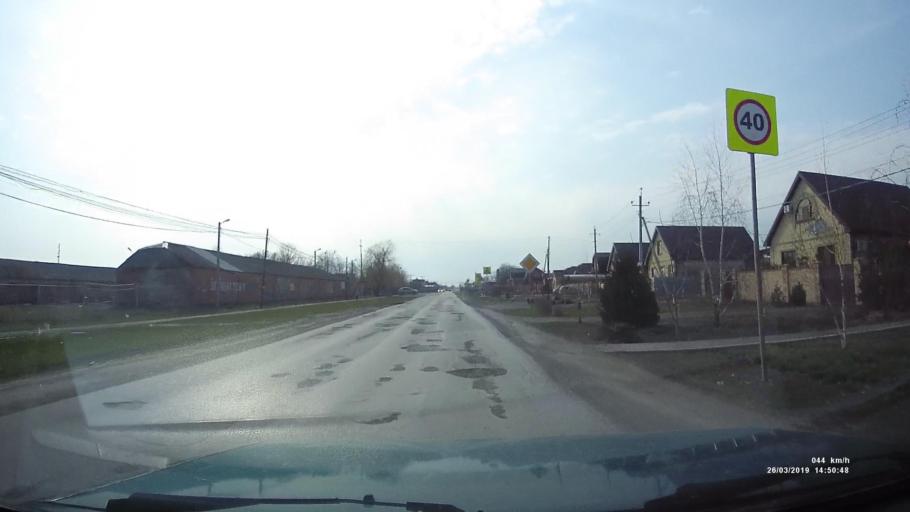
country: RU
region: Rostov
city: Novobessergenovka
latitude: 47.1857
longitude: 38.8341
